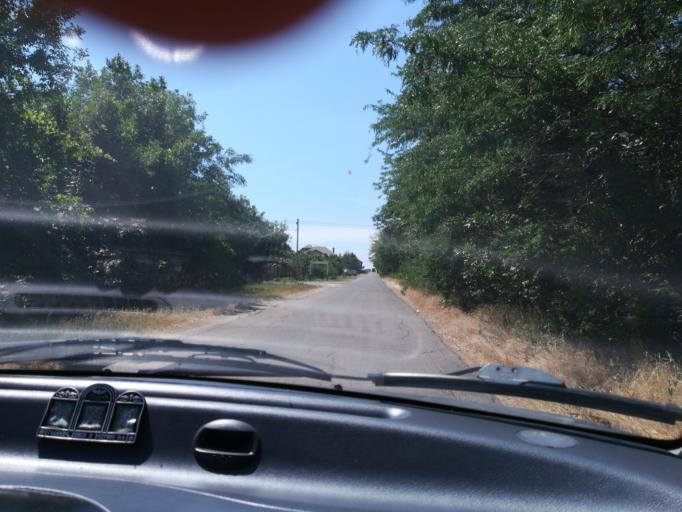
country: RU
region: Krasnodarskiy
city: Blagovetschenskaya
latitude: 45.0556
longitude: 37.1146
